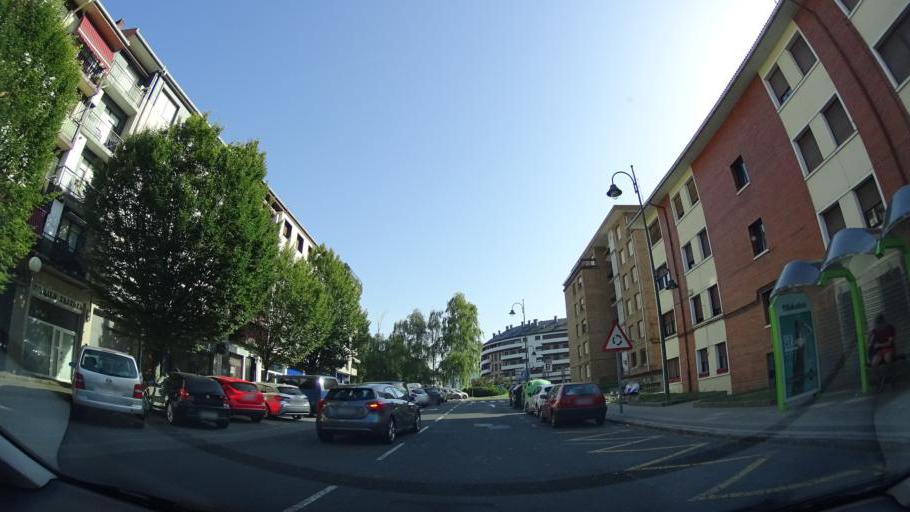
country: ES
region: Basque Country
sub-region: Bizkaia
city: Gernika-Lumo
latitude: 43.3065
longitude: -2.6813
